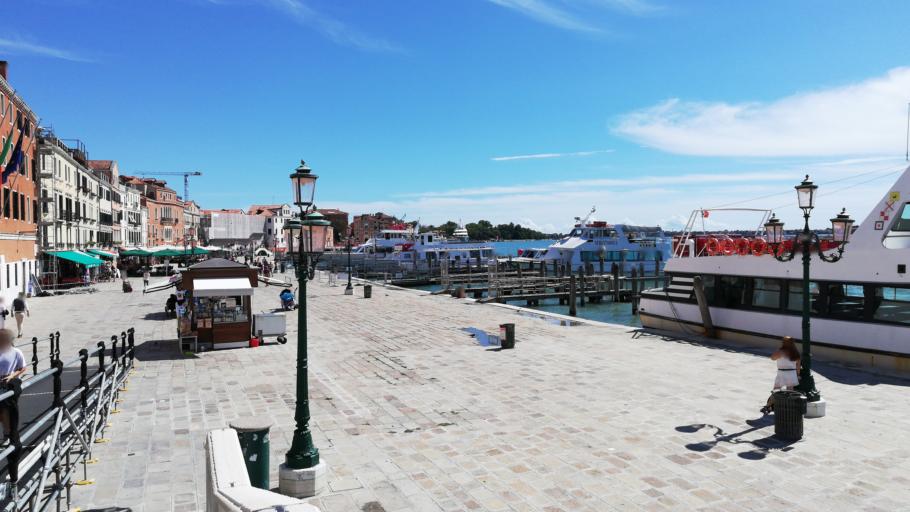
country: IT
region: Veneto
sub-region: Provincia di Venezia
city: Venice
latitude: 45.4339
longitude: 12.3454
